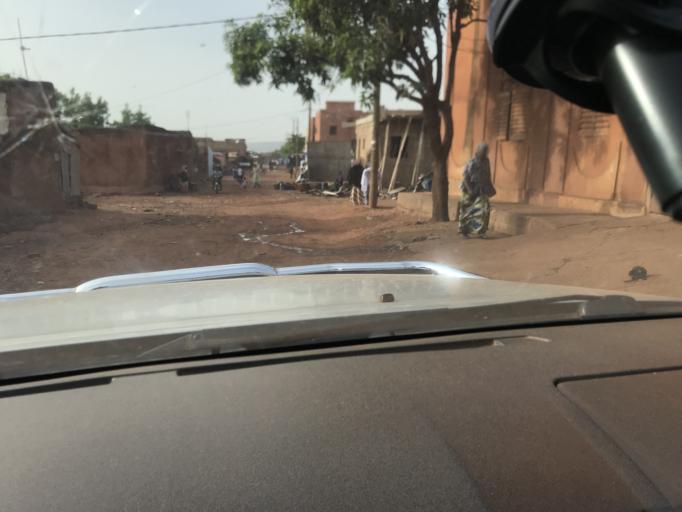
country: ML
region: Bamako
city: Bamako
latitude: 12.5942
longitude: -8.0076
